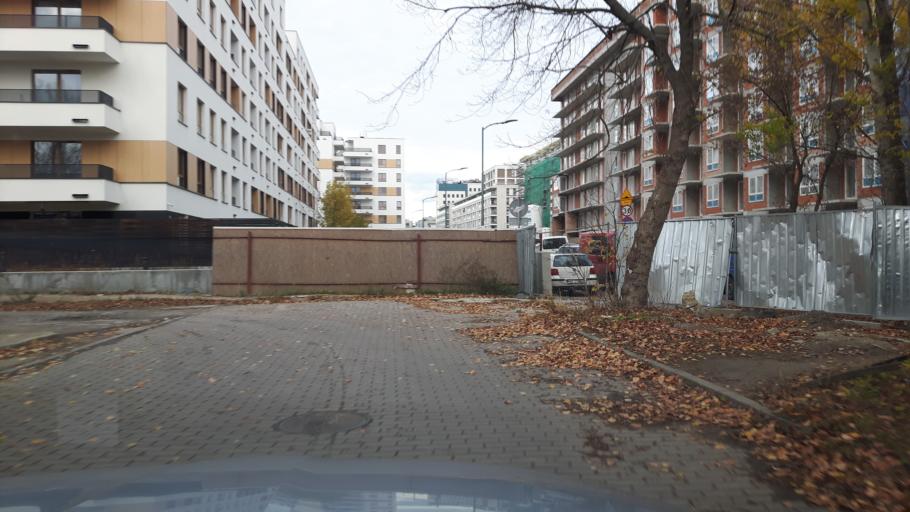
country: PL
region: Masovian Voivodeship
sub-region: Warszawa
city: Wlochy
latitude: 52.1750
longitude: 20.9908
